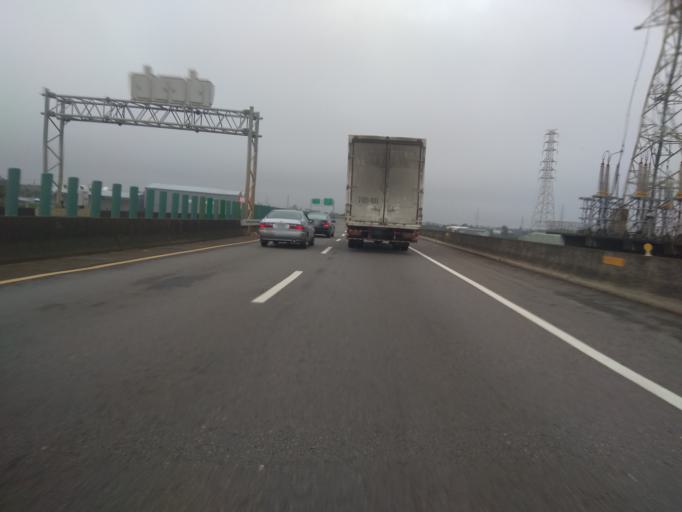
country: TW
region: Taiwan
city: Taoyuan City
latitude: 24.9819
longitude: 121.1314
